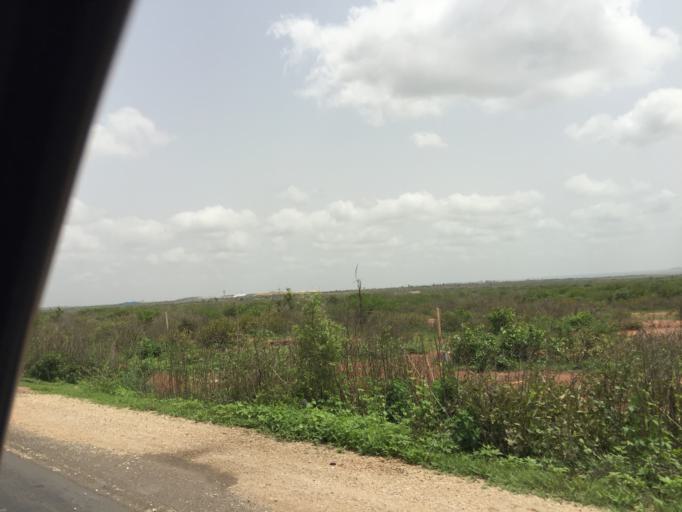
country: SN
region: Thies
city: Nguekhokh
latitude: 14.6314
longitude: -17.0639
